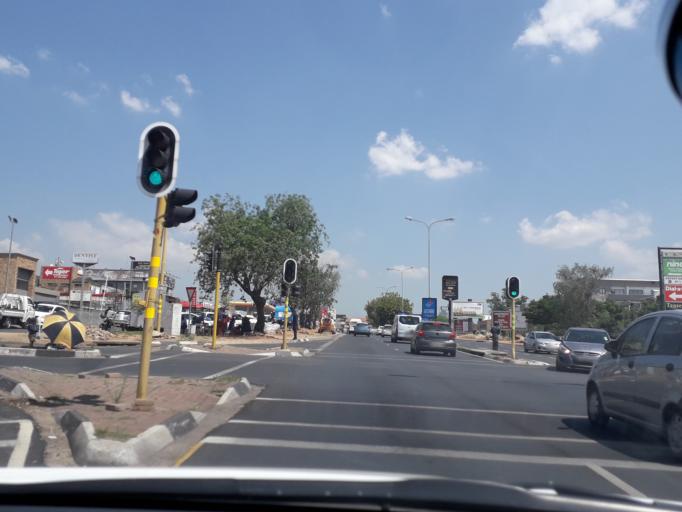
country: ZA
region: Gauteng
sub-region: City of Johannesburg Metropolitan Municipality
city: Midrand
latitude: -26.0573
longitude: 28.0592
